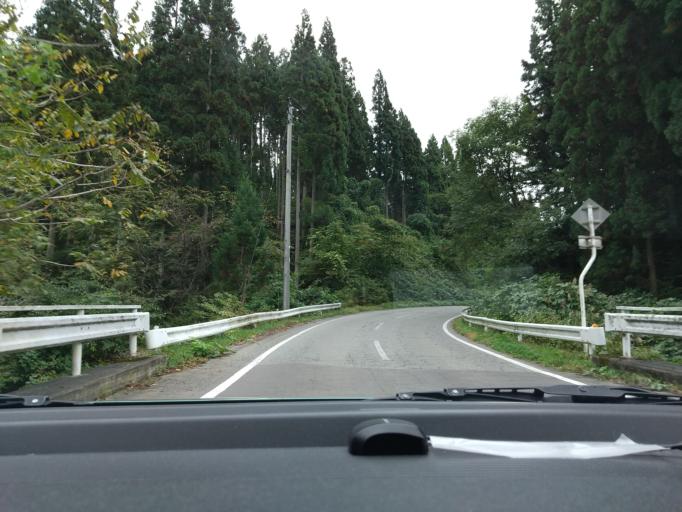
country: JP
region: Akita
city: Kakunodatemachi
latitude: 39.5417
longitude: 140.6411
